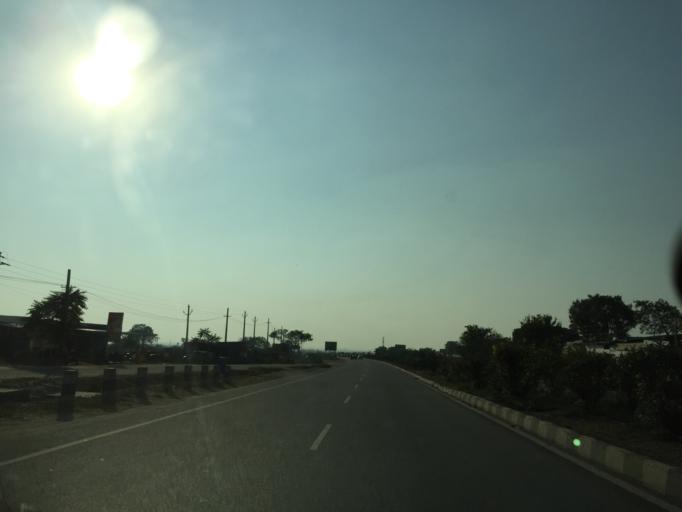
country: IN
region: Telangana
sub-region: Nalgonda
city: Bhongir
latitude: 17.5037
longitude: 78.8581
